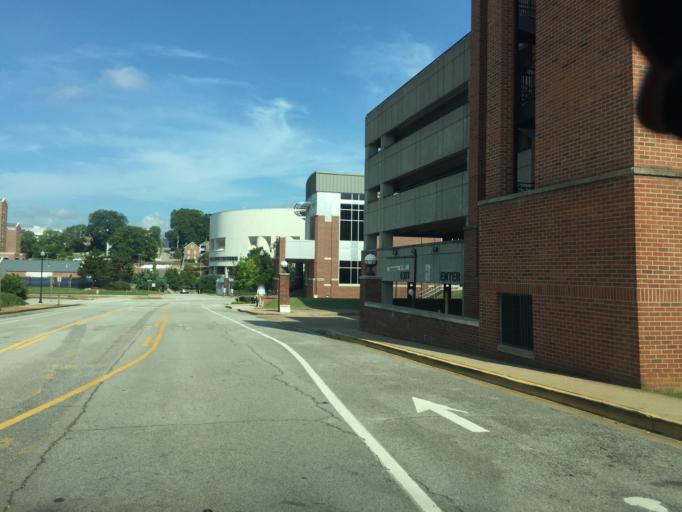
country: US
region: Tennessee
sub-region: Hamilton County
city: Chattanooga
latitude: 35.0490
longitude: -85.2989
